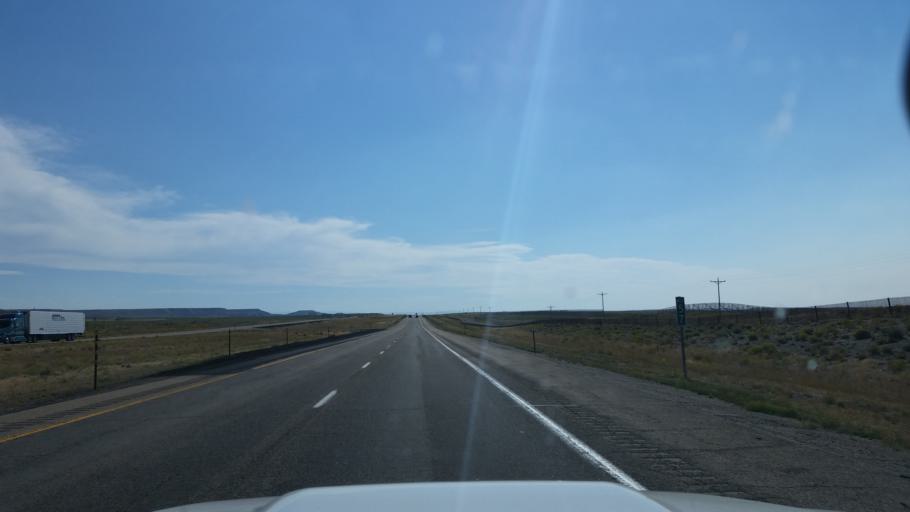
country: US
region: Wyoming
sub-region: Uinta County
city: Lyman
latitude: 41.4646
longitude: -110.0495
